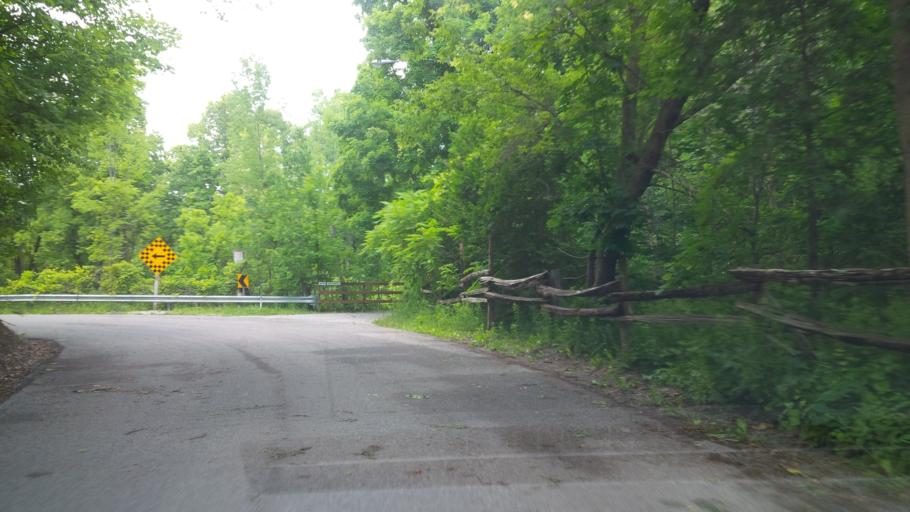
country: CA
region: Ontario
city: Burlington
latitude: 43.4318
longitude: -79.8619
